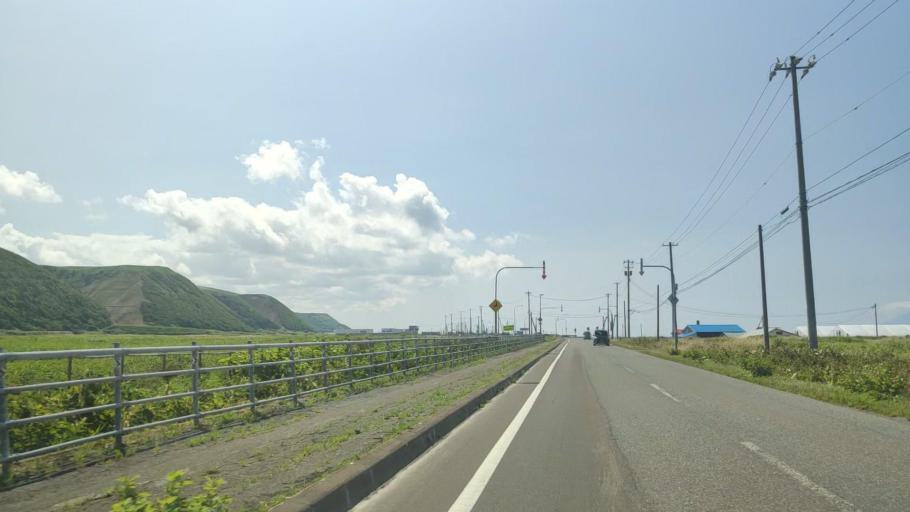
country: JP
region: Hokkaido
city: Wakkanai
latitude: 45.4365
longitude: 141.6411
